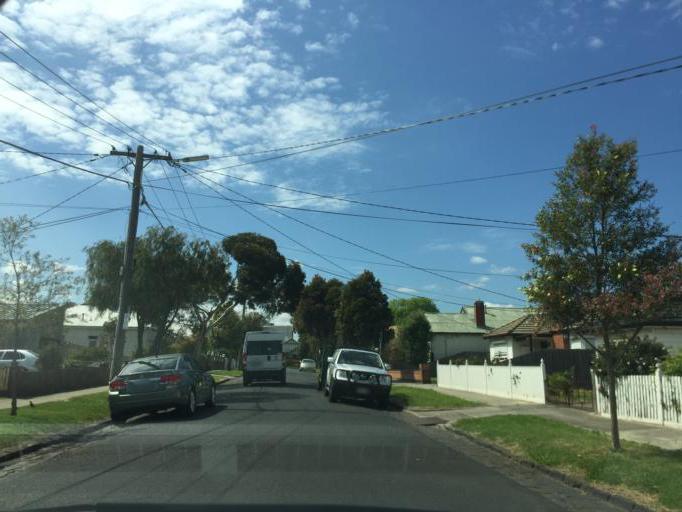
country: AU
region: Victoria
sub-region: Maribyrnong
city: West Footscray
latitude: -37.7929
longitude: 144.8828
